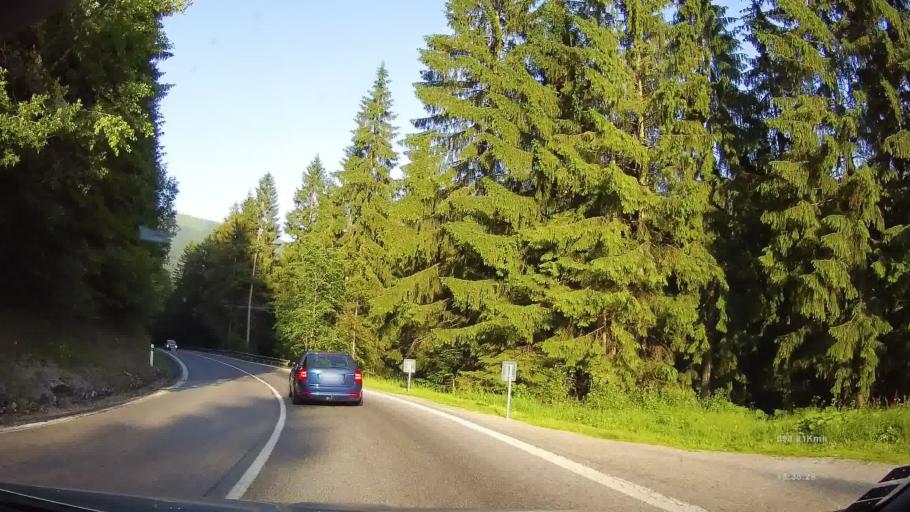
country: SK
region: Banskobystricky
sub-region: Okres Banska Bystrica
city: Brezno
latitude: 48.8936
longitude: 19.7025
